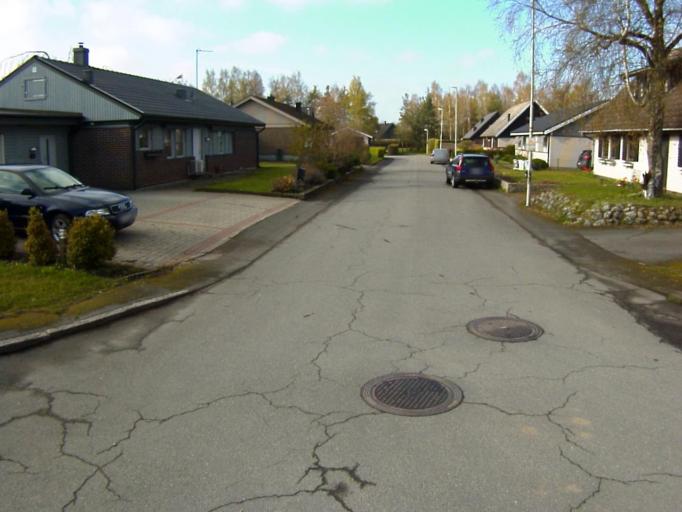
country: SE
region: Skane
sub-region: Kristianstads Kommun
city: Kristianstad
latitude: 56.0141
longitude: 14.1057
